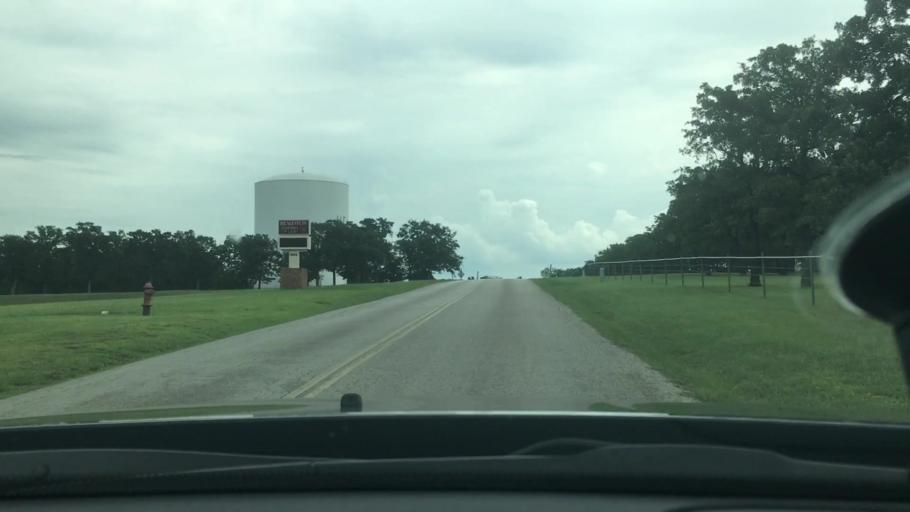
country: US
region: Oklahoma
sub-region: Carter County
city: Healdton
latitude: 34.2165
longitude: -97.4855
